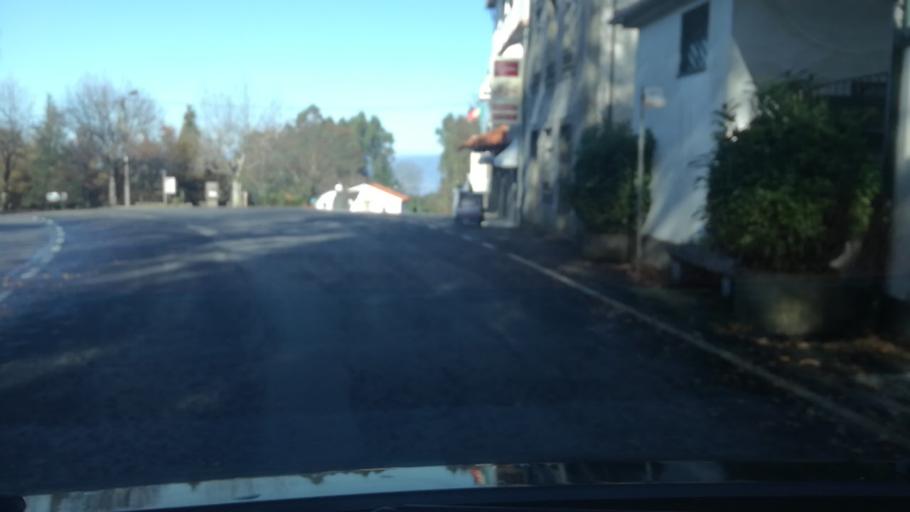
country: PT
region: Braga
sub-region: Braga
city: Braga
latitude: 41.5433
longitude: -8.3693
